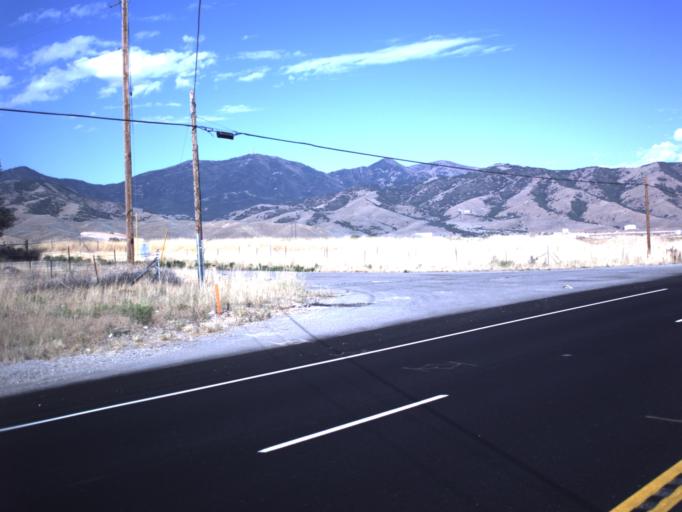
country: US
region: Utah
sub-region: Salt Lake County
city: Oquirrh
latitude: 40.6461
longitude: -112.0673
